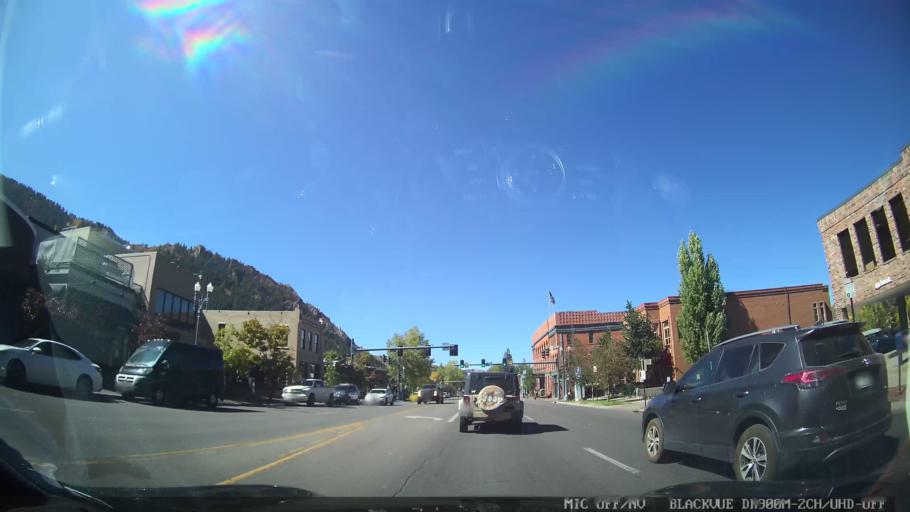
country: US
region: Colorado
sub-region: Pitkin County
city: Aspen
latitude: 39.1906
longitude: -106.8186
